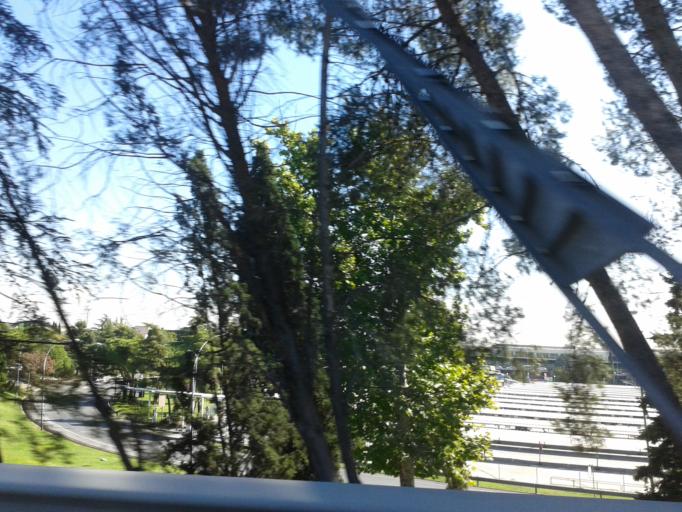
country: ES
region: Madrid
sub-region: Provincia de Madrid
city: Barajas de Madrid
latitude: 40.4657
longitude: -3.5739
